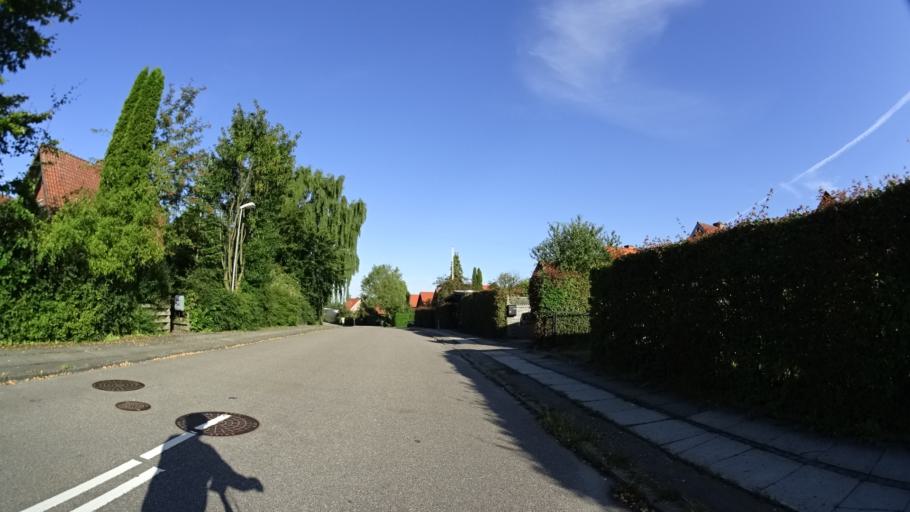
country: DK
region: Central Jutland
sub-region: Arhus Kommune
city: Stavtrup
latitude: 56.1205
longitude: 10.1679
